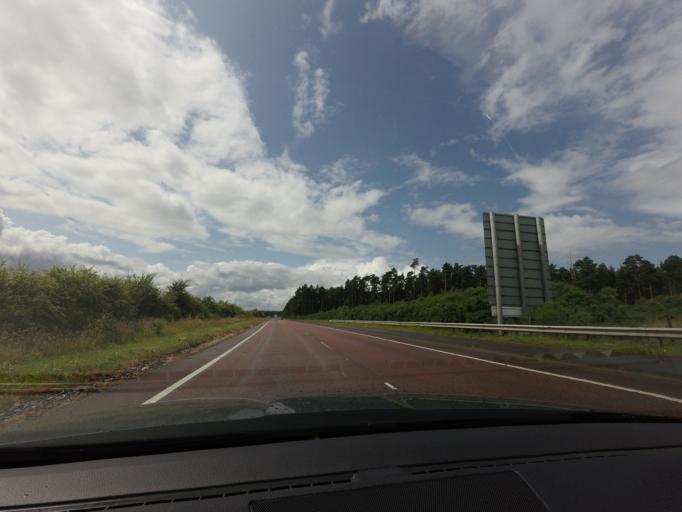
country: GB
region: Scotland
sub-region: Moray
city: Fochabers
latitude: 57.6266
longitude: -3.1455
